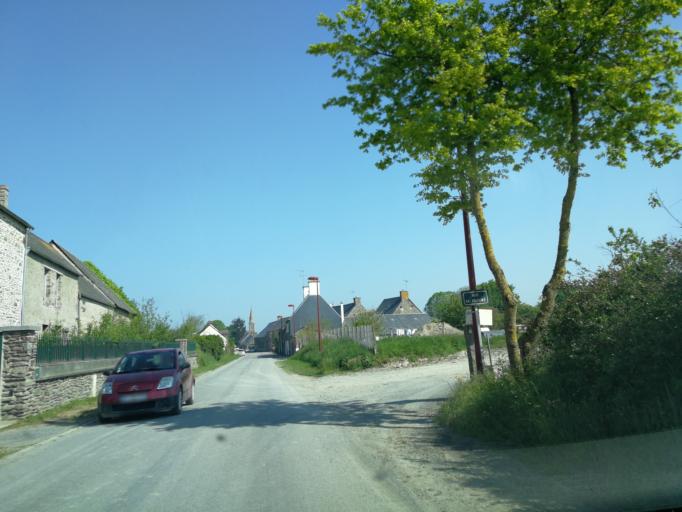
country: FR
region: Lower Normandy
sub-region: Departement de la Manche
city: Pontorson
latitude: 48.5990
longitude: -1.4732
